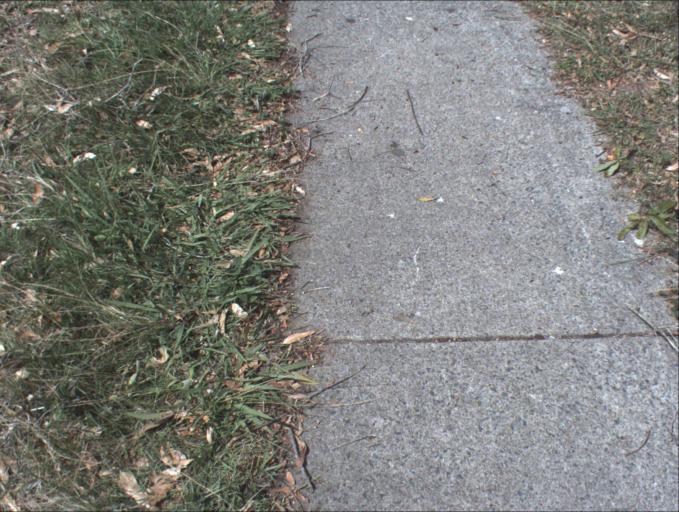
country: AU
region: Queensland
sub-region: Logan
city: Logan City
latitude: -27.6520
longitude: 153.1233
